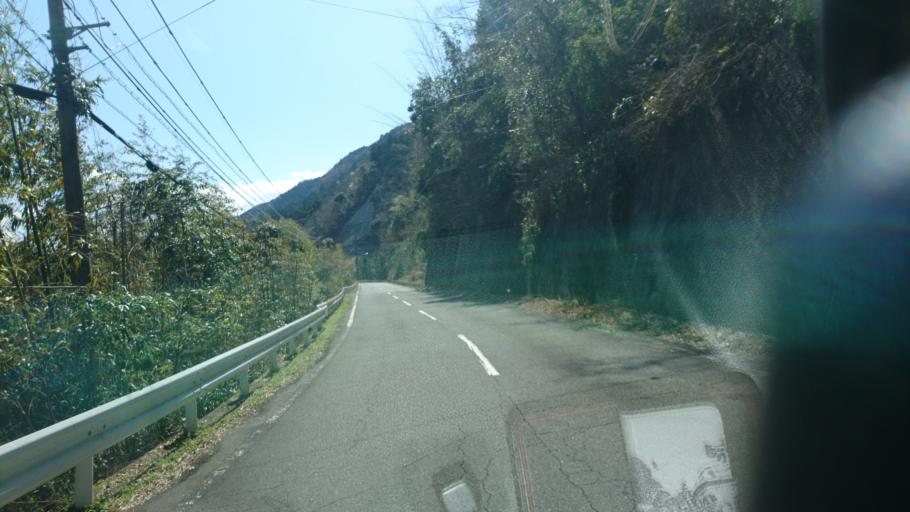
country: JP
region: Shizuoka
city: Fujinomiya
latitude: 35.3570
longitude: 138.4393
